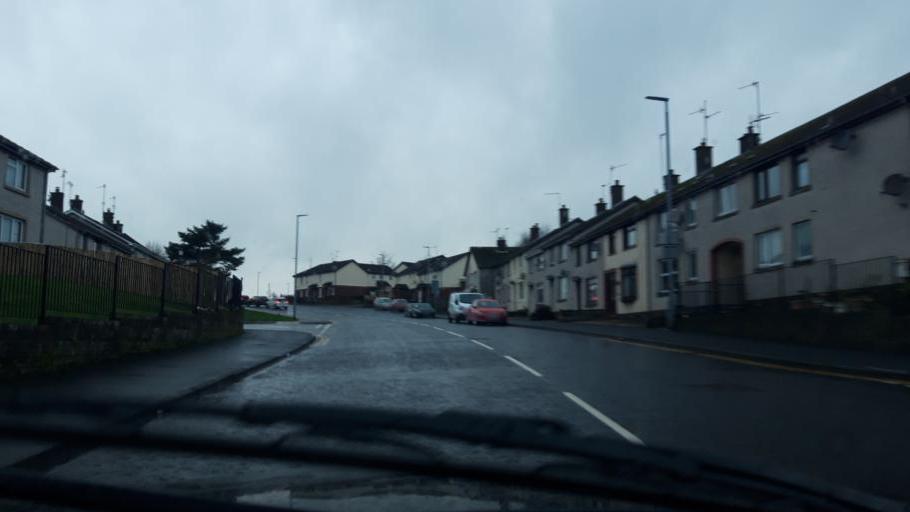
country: GB
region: Northern Ireland
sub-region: Banbridge District
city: Banbridge
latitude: 54.3508
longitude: -6.2747
